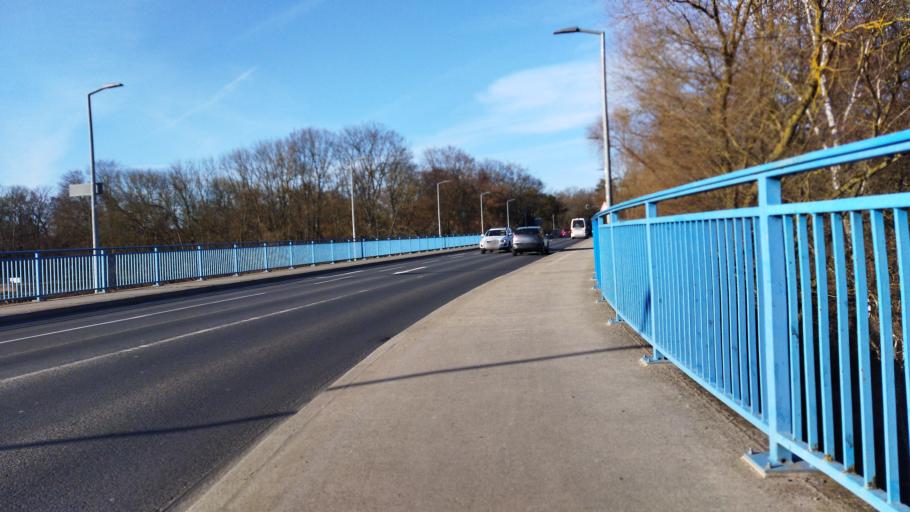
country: DE
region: Bavaria
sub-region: Regierungsbezirk Unterfranken
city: Sennfeld
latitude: 50.0392
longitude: 10.2401
